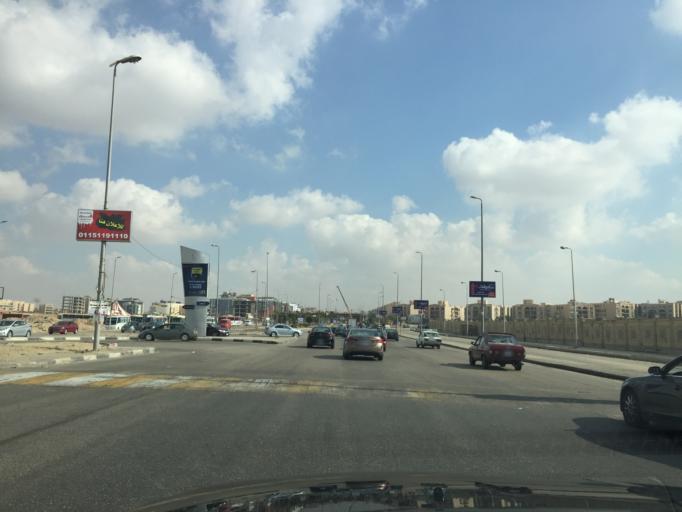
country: EG
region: Muhafazat al Qalyubiyah
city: Al Khankah
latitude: 30.0254
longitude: 31.4712
